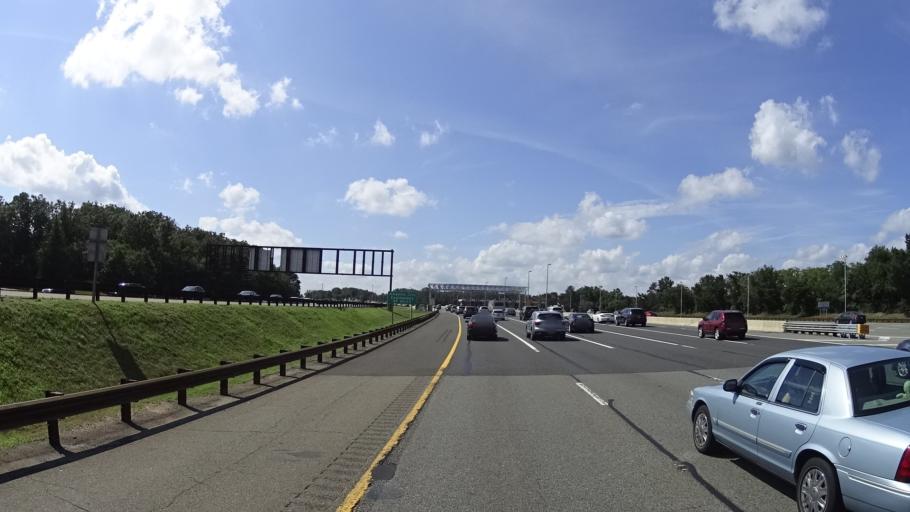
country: US
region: New Jersey
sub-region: Middlesex County
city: South Amboy
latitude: 40.4882
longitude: -74.3025
